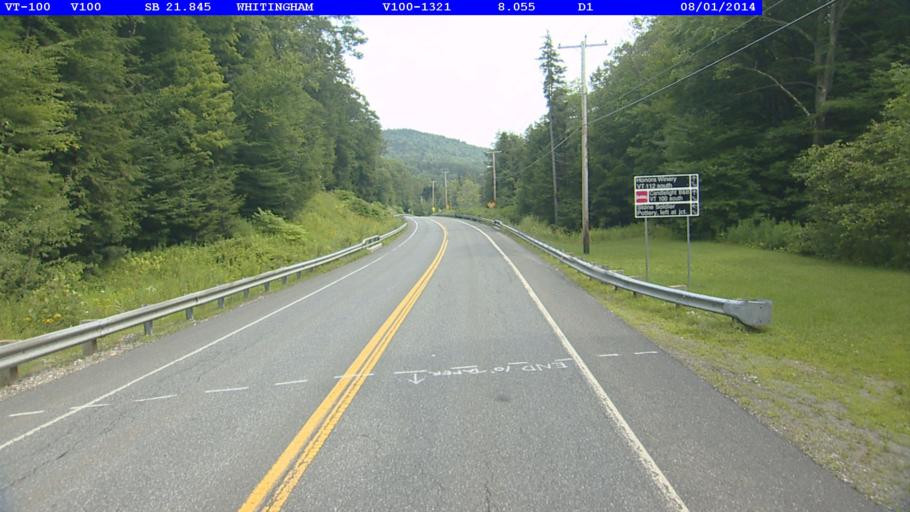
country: US
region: Vermont
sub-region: Windham County
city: Dover
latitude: 42.8011
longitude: -72.8257
